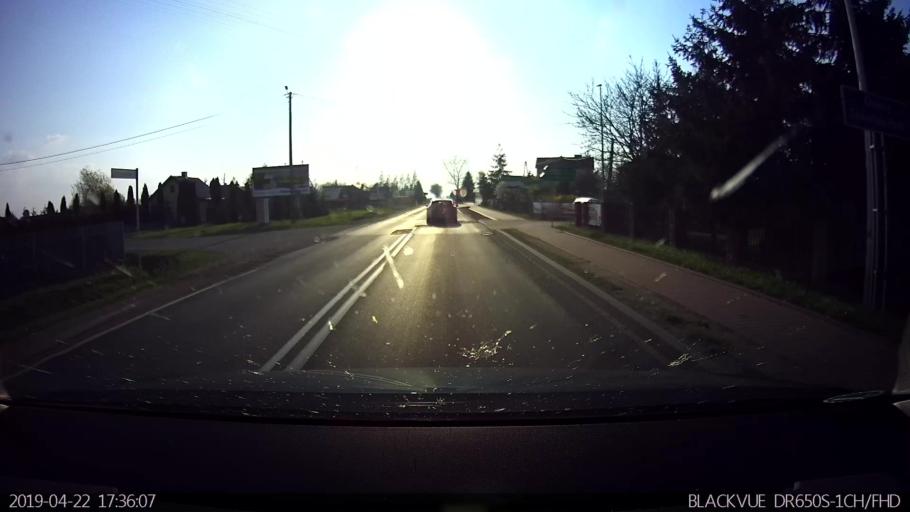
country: PL
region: Masovian Voivodeship
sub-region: Powiat sokolowski
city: Sokolow Podlaski
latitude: 52.4074
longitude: 22.1938
